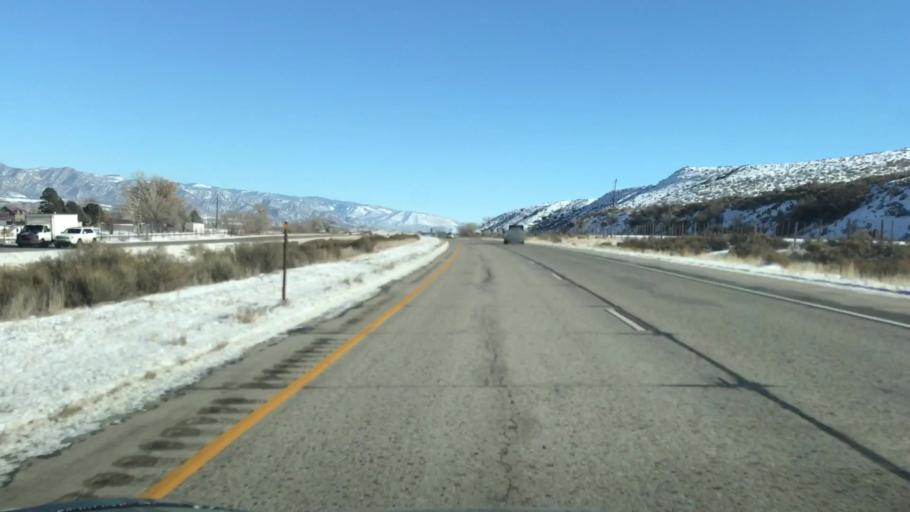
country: US
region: Colorado
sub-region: Garfield County
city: Rifle
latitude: 39.5308
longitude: -107.7254
